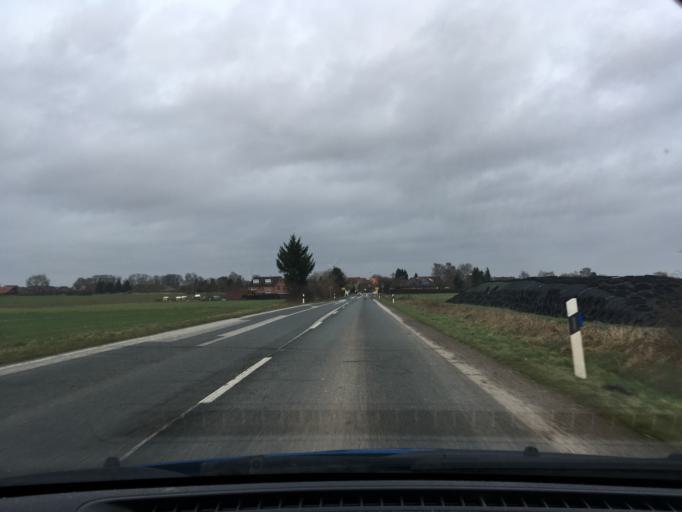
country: DE
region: Schleswig-Holstein
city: Lutau
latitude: 53.4286
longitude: 10.5424
